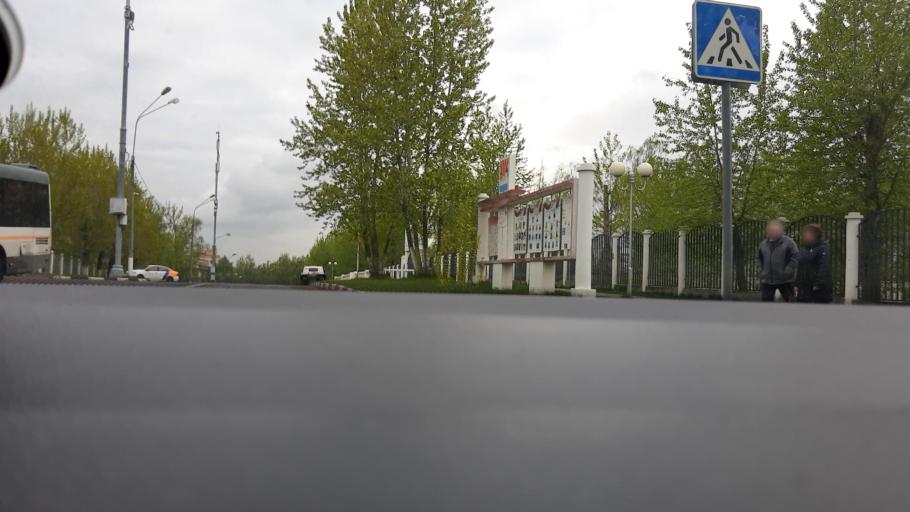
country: RU
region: Moskovskaya
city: Kotel'niki
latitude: 55.6290
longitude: 37.8484
